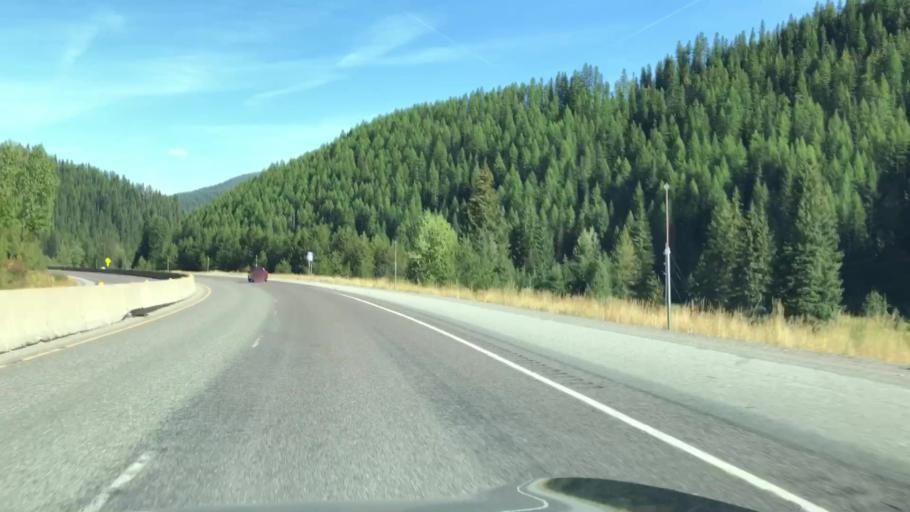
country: US
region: Montana
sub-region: Sanders County
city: Thompson Falls
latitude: 47.4190
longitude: -115.6007
